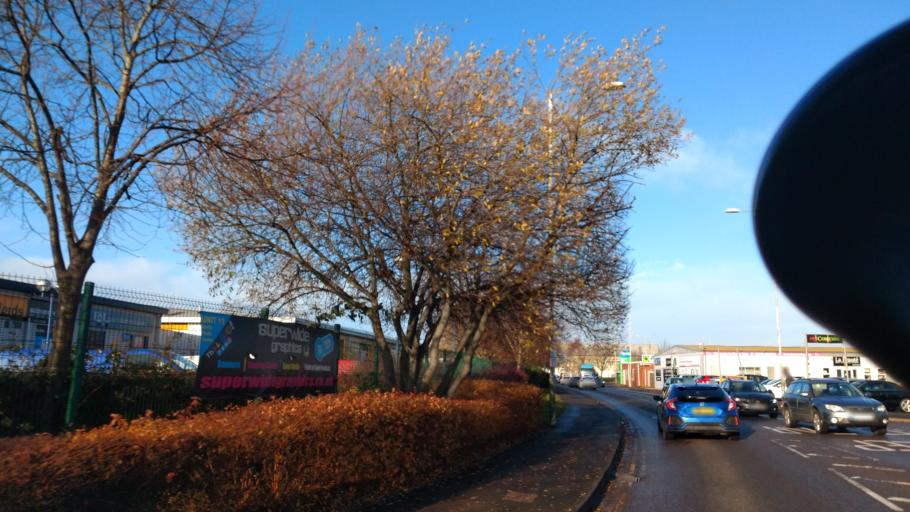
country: GB
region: England
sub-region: Borough of Swindon
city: Swindon
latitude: 51.5820
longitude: -1.7509
